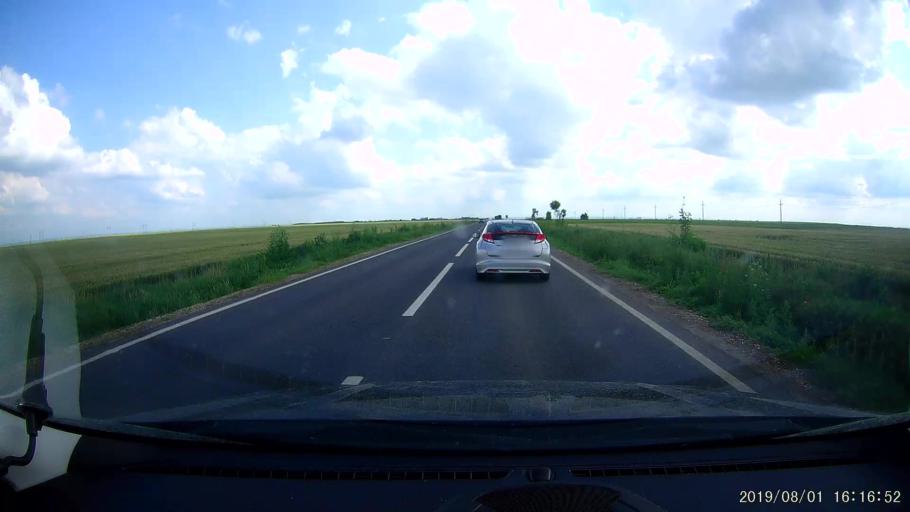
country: RO
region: Calarasi
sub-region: Comuna Stefan Voda
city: Stefan Voda
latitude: 44.3131
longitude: 27.3567
